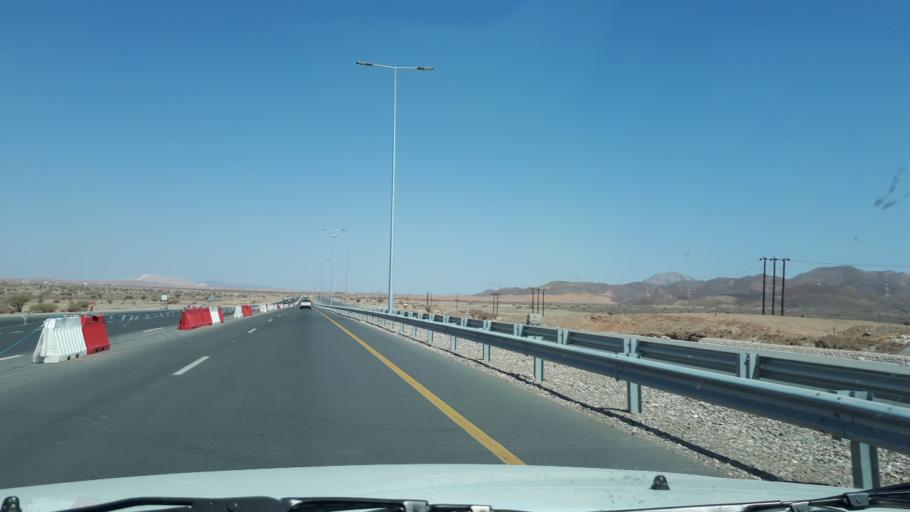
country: OM
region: Ash Sharqiyah
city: Badiyah
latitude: 22.4857
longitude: 58.9767
